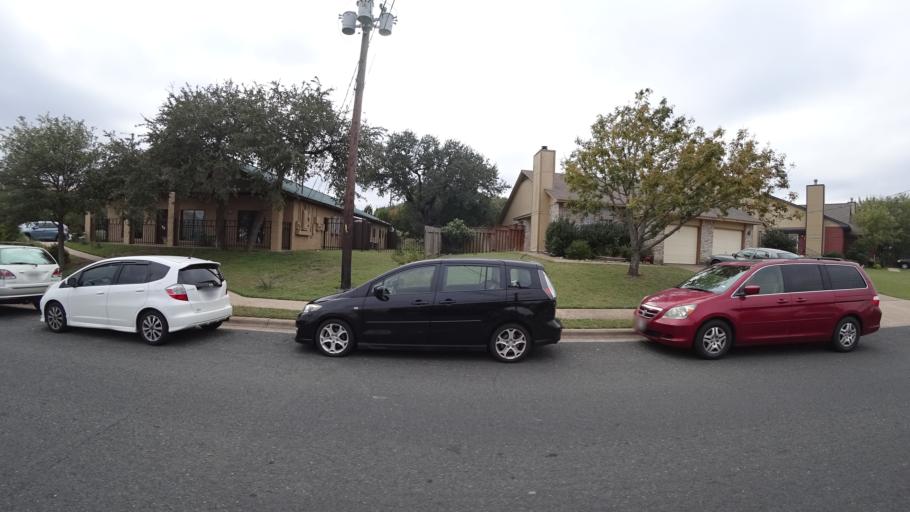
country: US
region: Texas
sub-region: Travis County
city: Barton Creek
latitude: 30.2337
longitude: -97.8776
